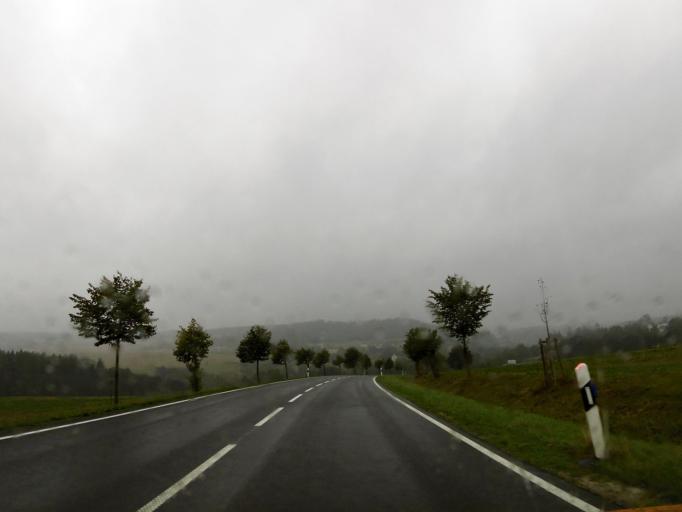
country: DE
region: Saxony-Anhalt
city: Friedrichsbrunn
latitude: 51.6475
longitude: 10.9981
